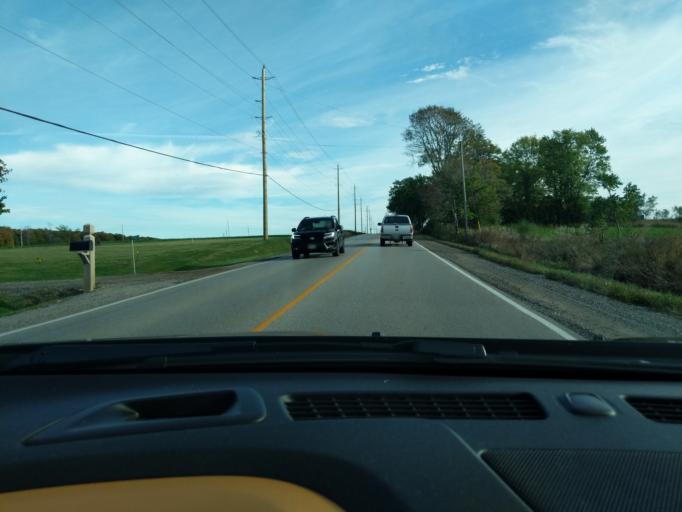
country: CA
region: Ontario
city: Barrie
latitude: 44.4186
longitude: -79.7572
